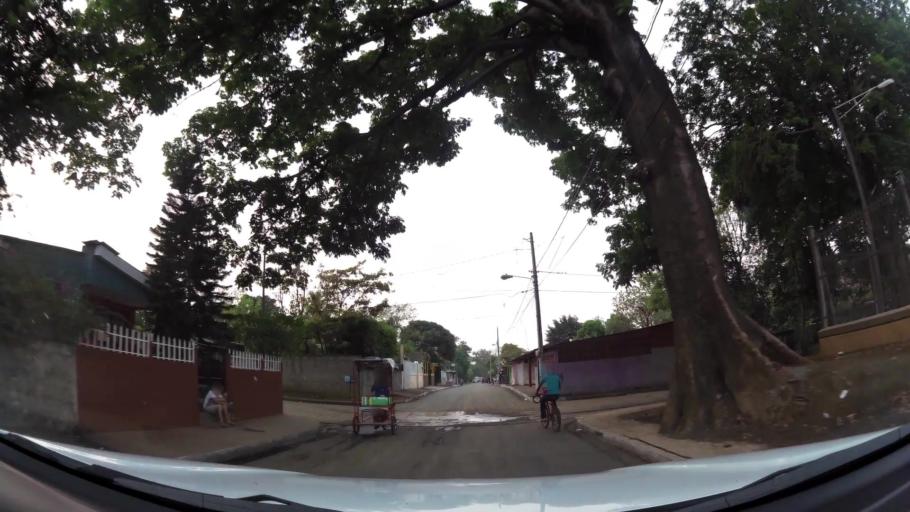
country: NI
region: Masaya
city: Nindiri
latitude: 12.0034
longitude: -86.1239
